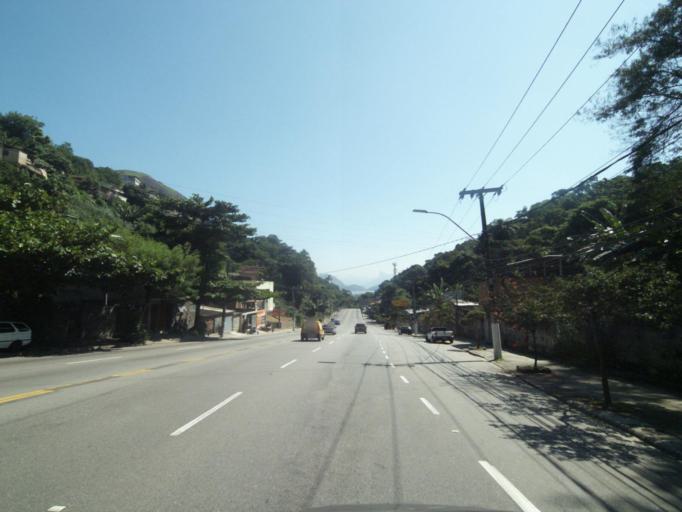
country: BR
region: Rio de Janeiro
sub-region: Niteroi
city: Niteroi
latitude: -22.9105
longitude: -43.0706
